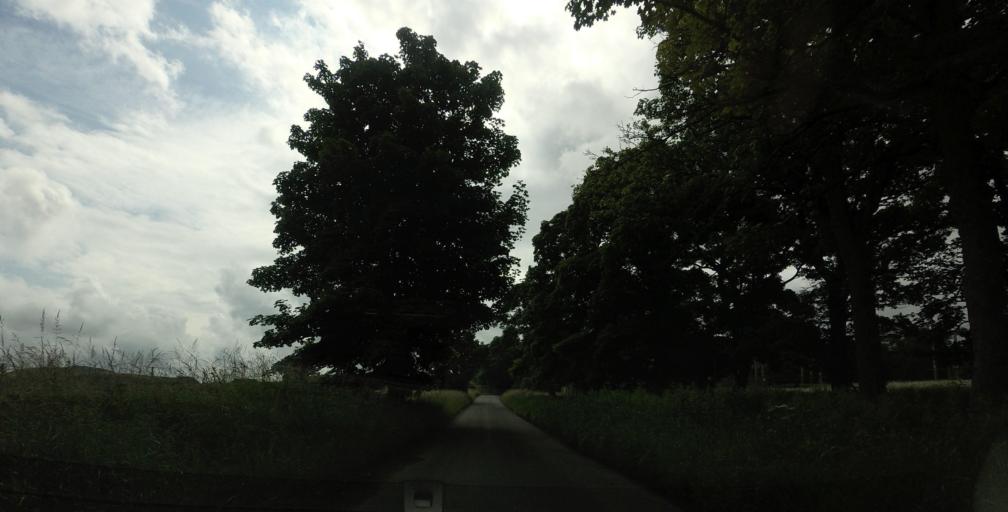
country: GB
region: Scotland
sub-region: West Lothian
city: Kirknewton
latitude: 55.8899
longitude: -3.4048
